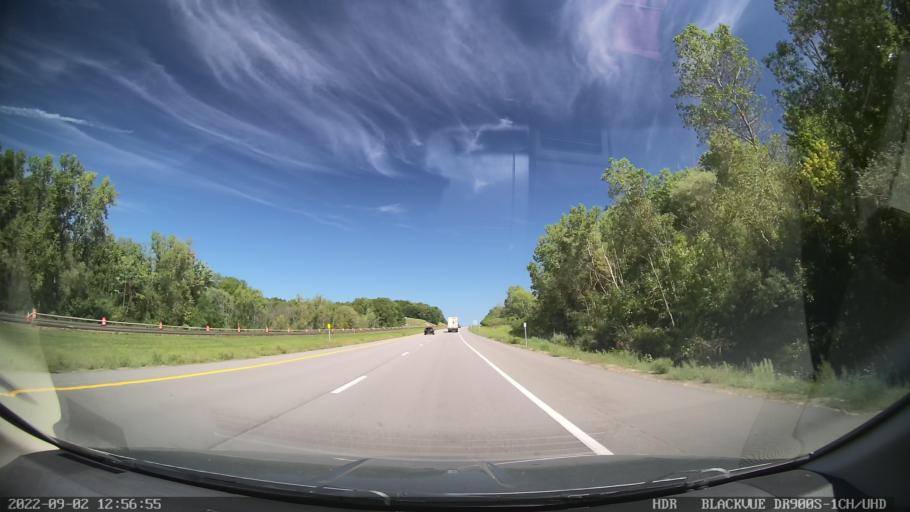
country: US
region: New York
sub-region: Livingston County
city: Avon
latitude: 42.9649
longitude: -77.6926
